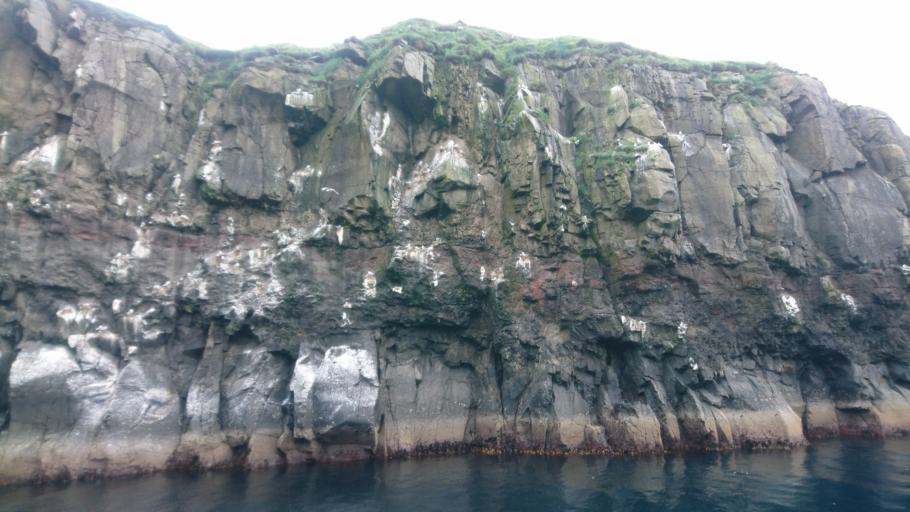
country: FO
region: Vagar
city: Sorvagur
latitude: 62.1019
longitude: -7.6479
